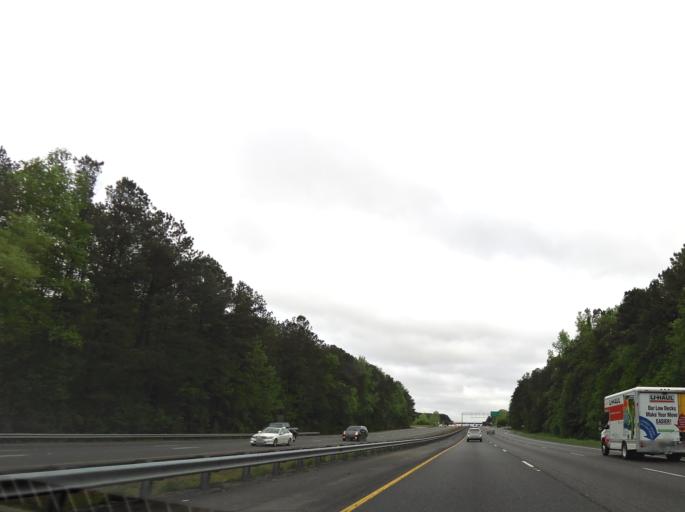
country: US
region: Georgia
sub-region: Butts County
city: Indian Springs
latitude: 33.1721
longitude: -84.0433
